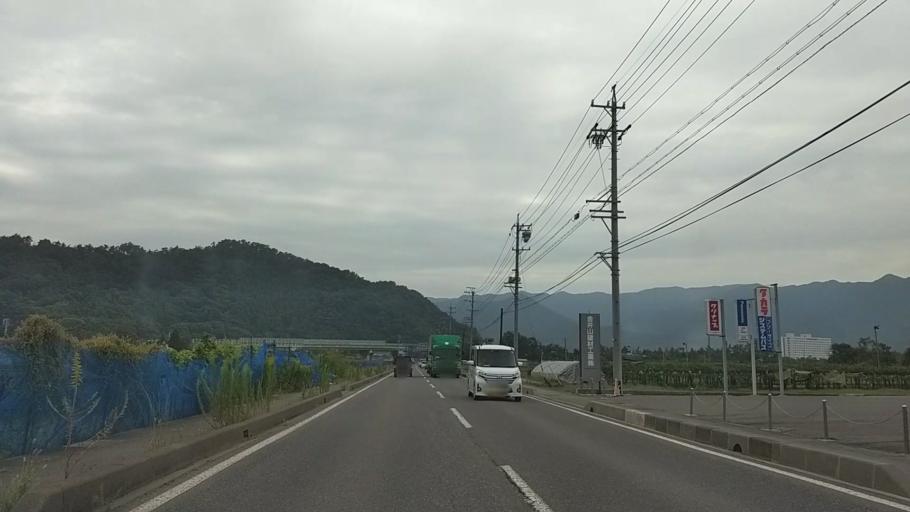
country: JP
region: Nagano
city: Nagano-shi
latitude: 36.5815
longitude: 138.2016
